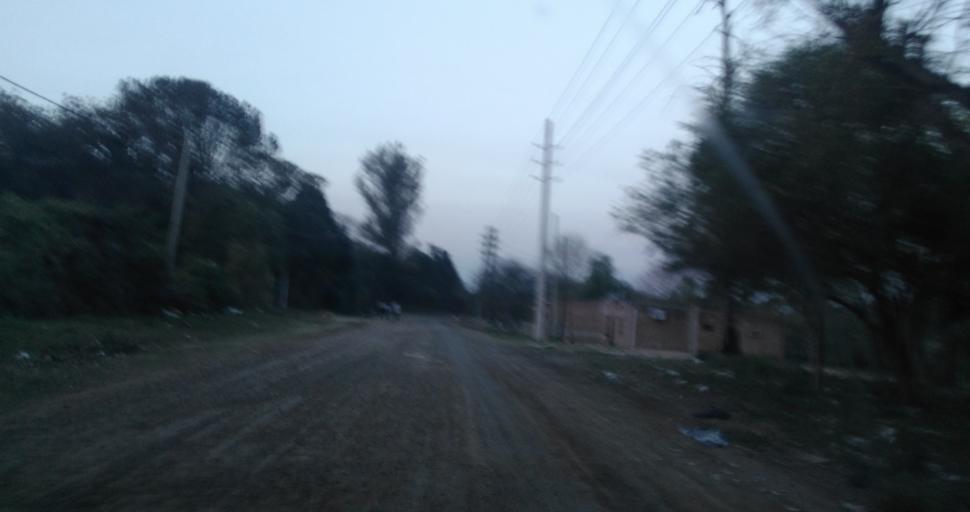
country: AR
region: Chaco
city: Fontana
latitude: -27.4269
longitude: -58.9933
